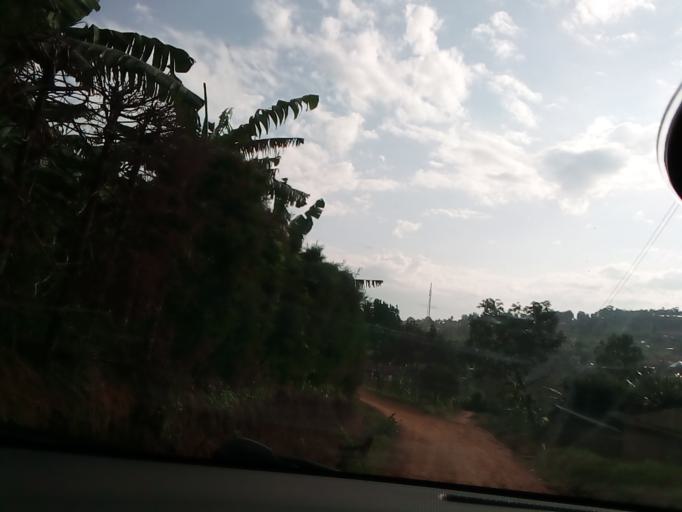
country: UG
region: Central Region
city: Masaka
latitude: -0.3542
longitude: 31.7450
